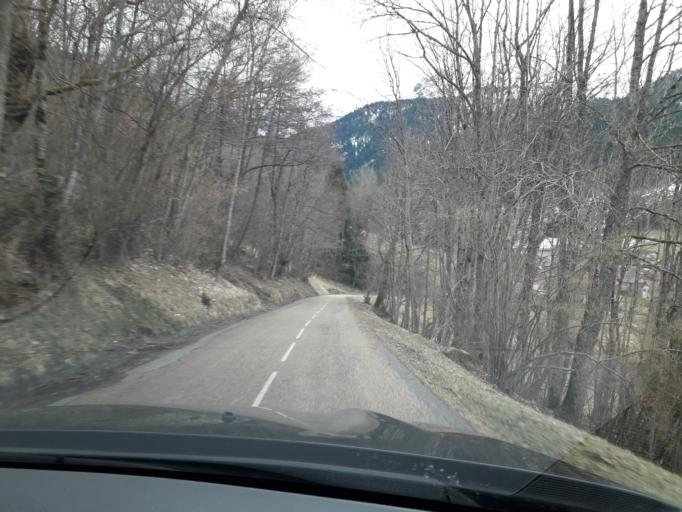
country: FR
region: Rhone-Alpes
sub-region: Departement de l'Isere
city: Le Champ-pres-Froges
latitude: 45.2418
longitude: 5.9748
